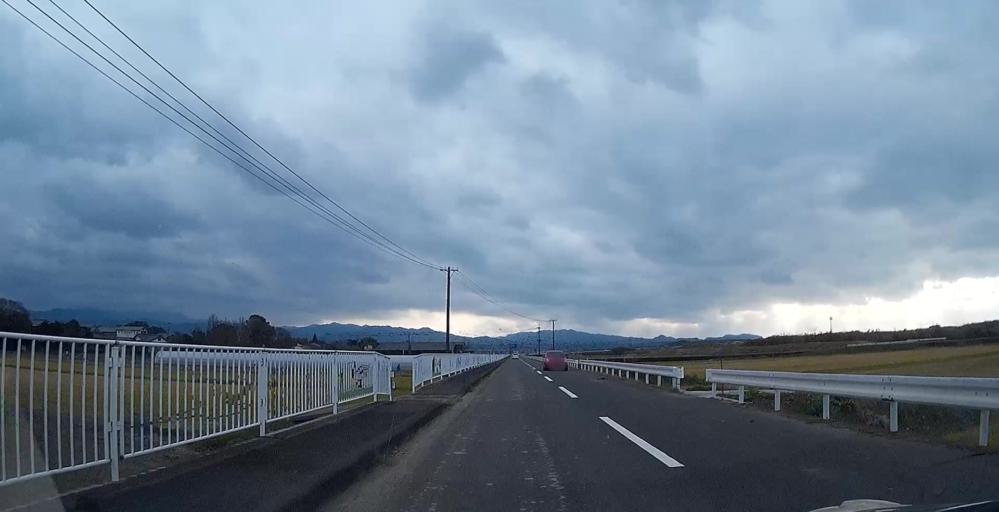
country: JP
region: Kagoshima
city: Izumi
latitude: 32.0877
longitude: 130.2765
